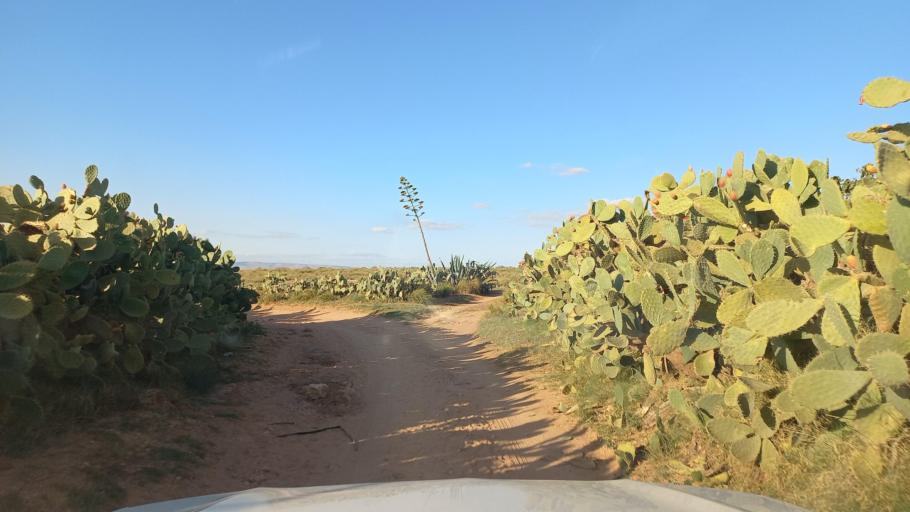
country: TN
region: Al Qasrayn
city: Sbiba
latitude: 35.3865
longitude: 9.1548
